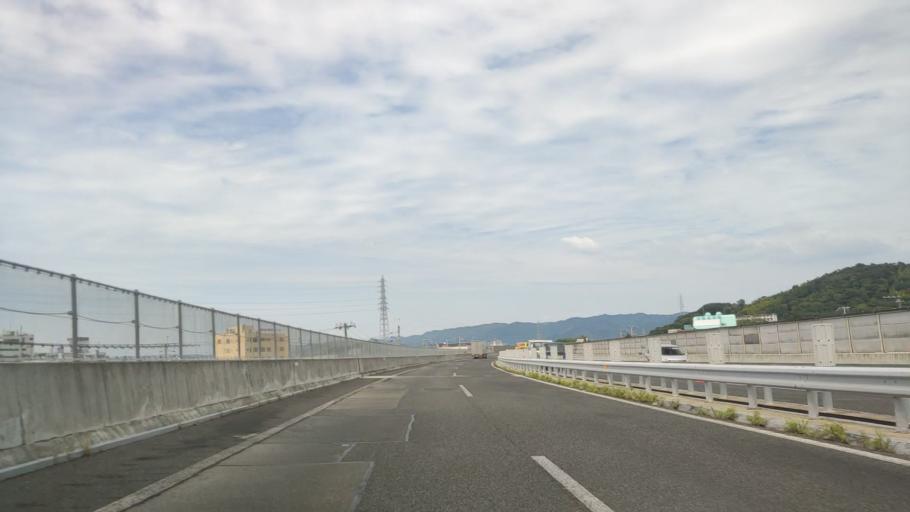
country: JP
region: Wakayama
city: Wakayama-shi
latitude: 34.2244
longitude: 135.2149
